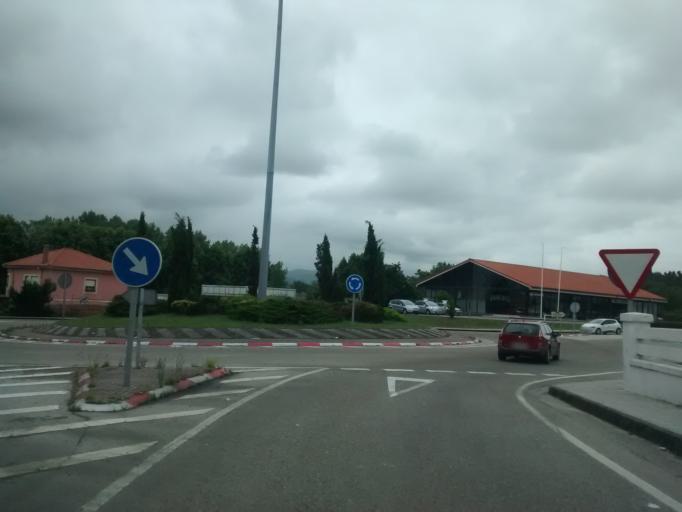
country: ES
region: Cantabria
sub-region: Provincia de Cantabria
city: Torrelavega
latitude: 43.3783
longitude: -4.0485
